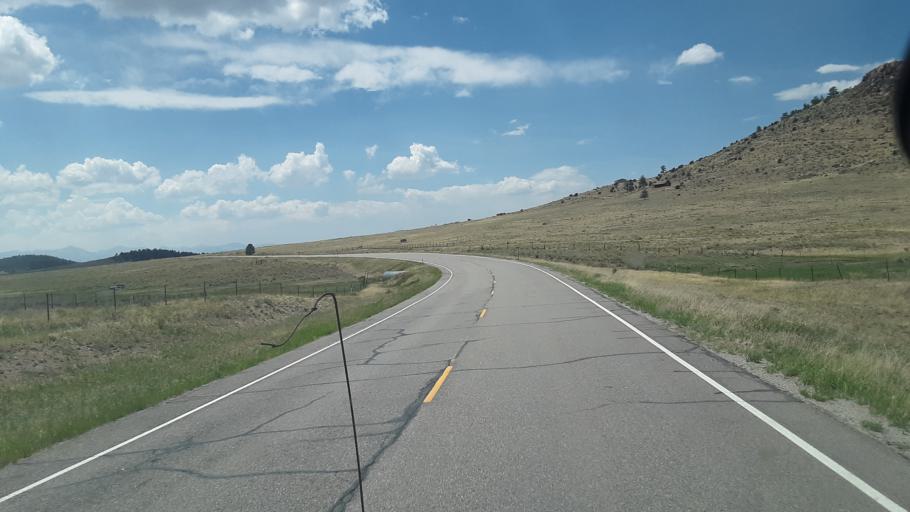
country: US
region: Colorado
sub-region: Custer County
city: Westcliffe
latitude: 38.1640
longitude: -105.2718
